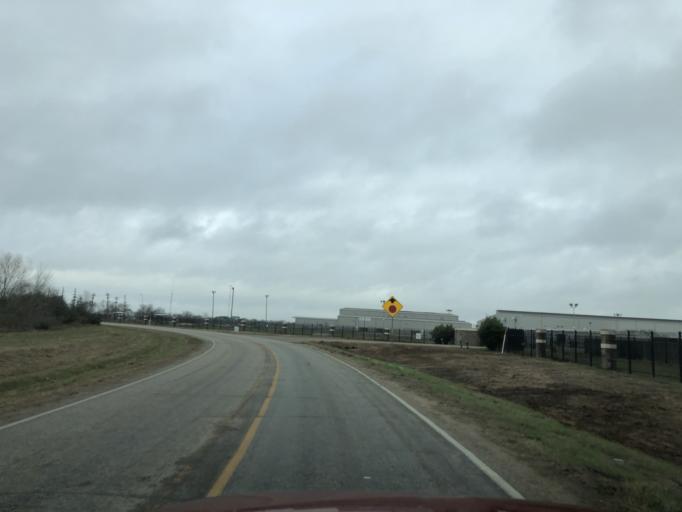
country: US
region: Texas
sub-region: Austin County
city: Sealy
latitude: 29.7604
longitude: -96.2191
